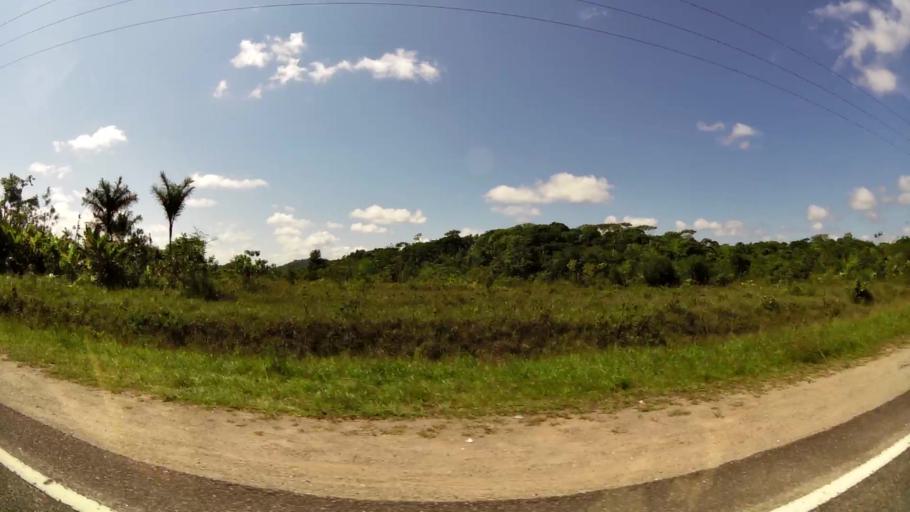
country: GF
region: Guyane
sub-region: Guyane
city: Matoury
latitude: 4.8301
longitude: -52.3522
